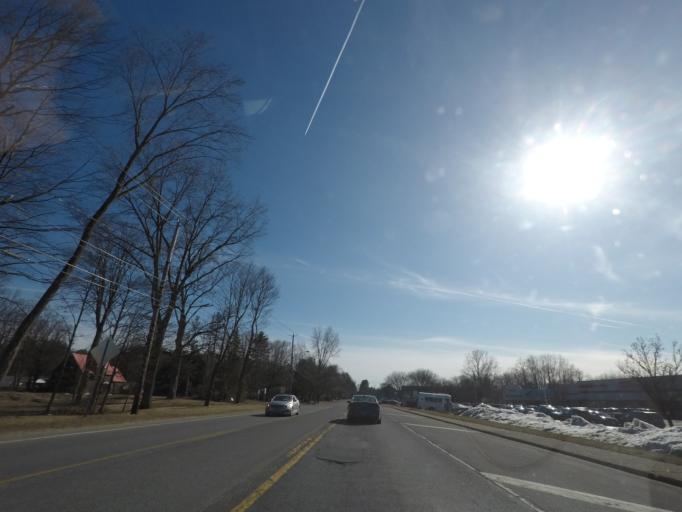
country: US
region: New York
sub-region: Saratoga County
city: Saratoga Springs
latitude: 43.0706
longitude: -73.7932
